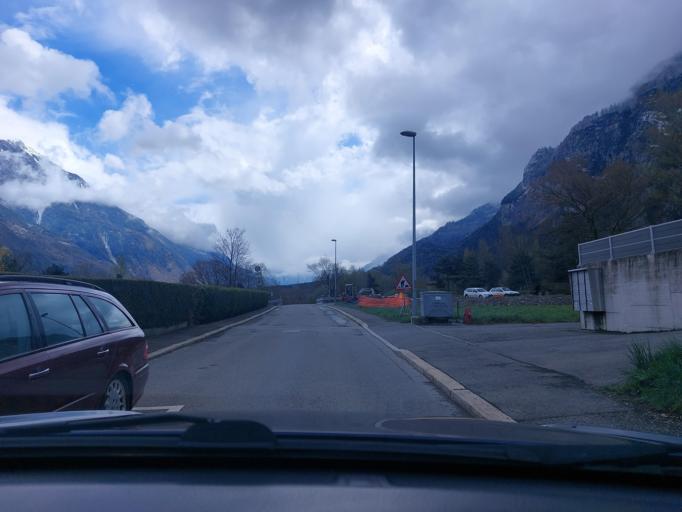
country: CH
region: Valais
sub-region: Saint-Maurice District
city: Saint-Maurice
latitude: 46.2092
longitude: 7.0025
